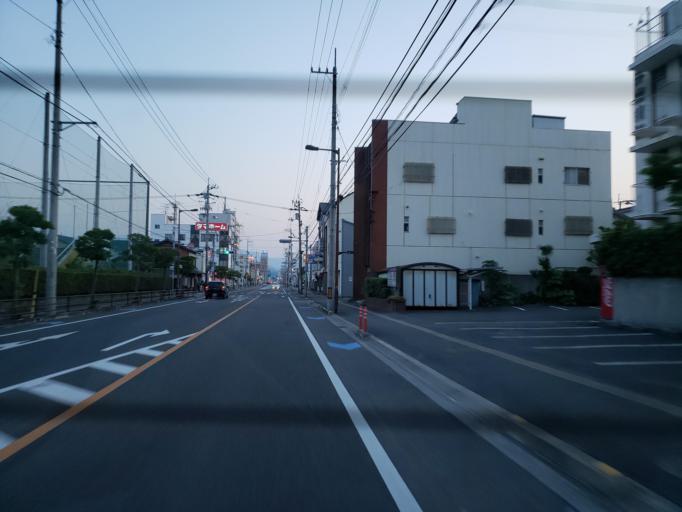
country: JP
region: Ehime
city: Hojo
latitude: 34.0555
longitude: 132.9881
